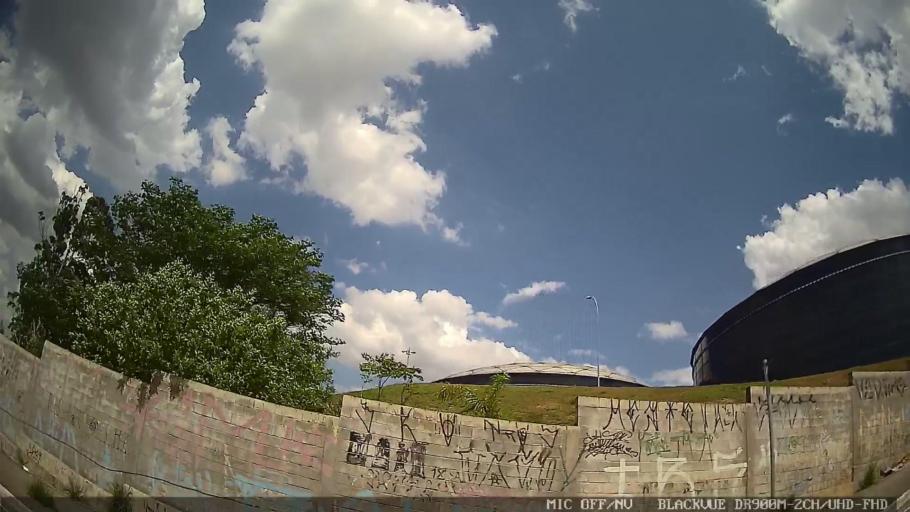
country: BR
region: Sao Paulo
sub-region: Sao Caetano Do Sul
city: Sao Caetano do Sul
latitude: -23.5508
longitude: -46.4783
